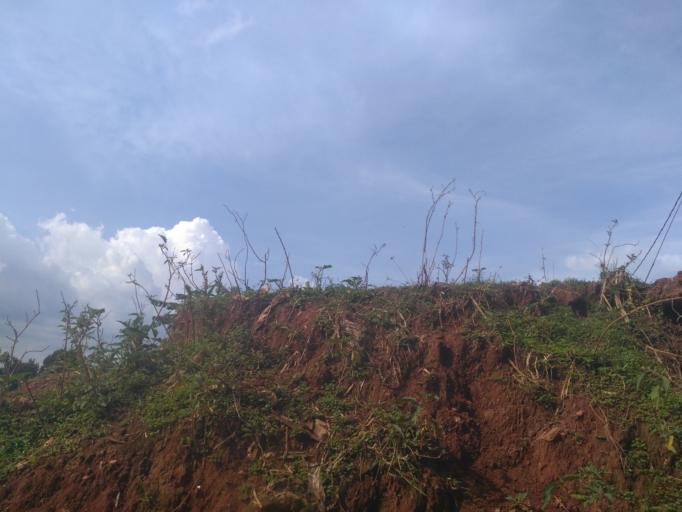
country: UG
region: Central Region
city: Kampala Central Division
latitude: 0.3627
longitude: 32.5602
